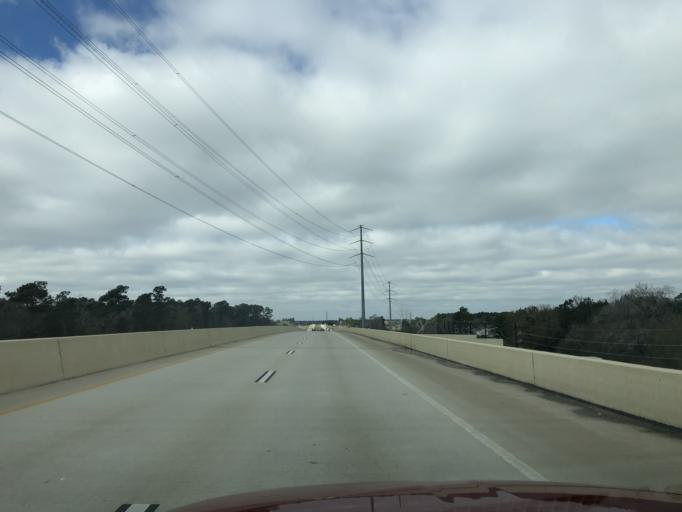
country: US
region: Texas
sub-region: Montgomery County
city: The Woodlands
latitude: 30.0944
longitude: -95.4929
